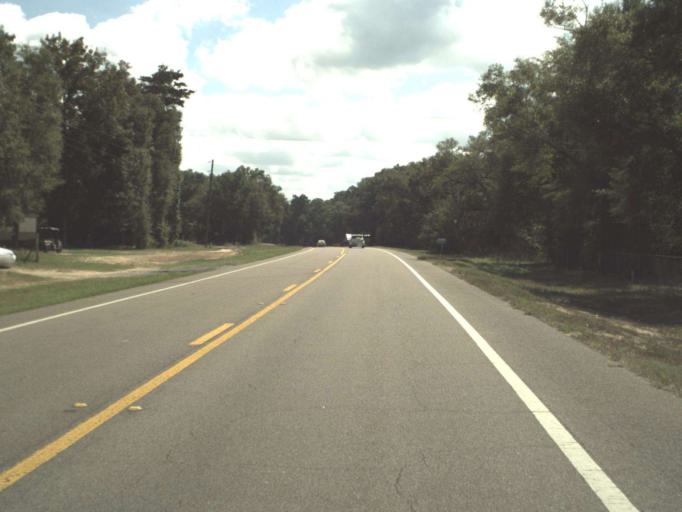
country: US
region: Florida
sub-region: Walton County
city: Freeport
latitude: 30.5829
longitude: -85.9349
